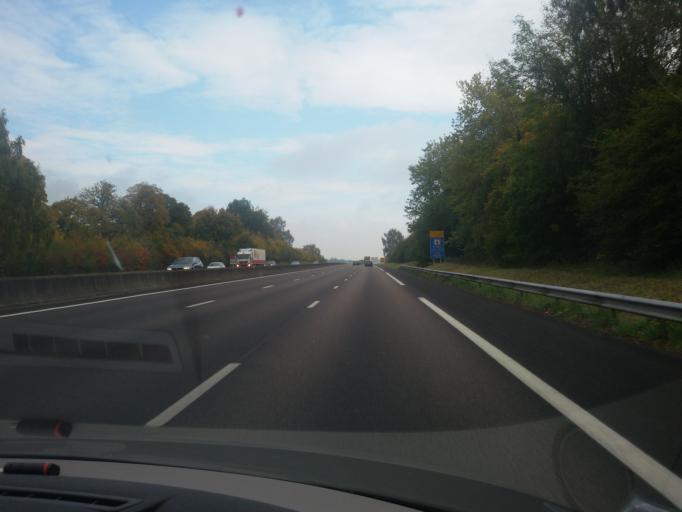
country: FR
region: Haute-Normandie
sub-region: Departement de l'Eure
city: Bourg-Achard
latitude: 49.3670
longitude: 0.7902
